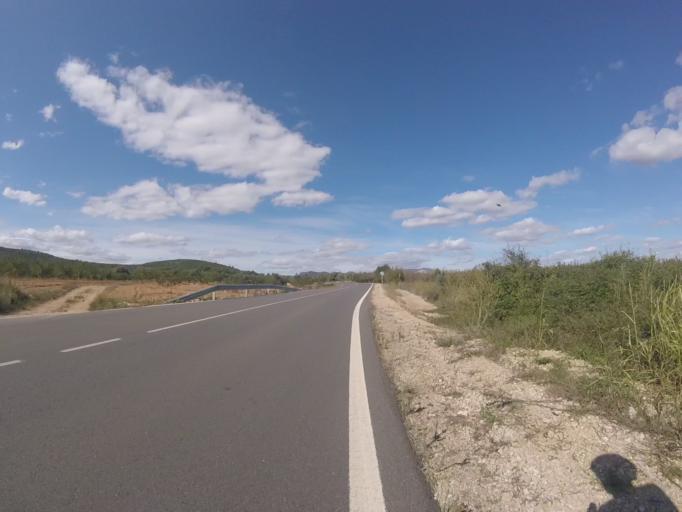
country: ES
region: Valencia
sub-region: Provincia de Castello
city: Chert/Xert
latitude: 40.4291
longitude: 0.1423
